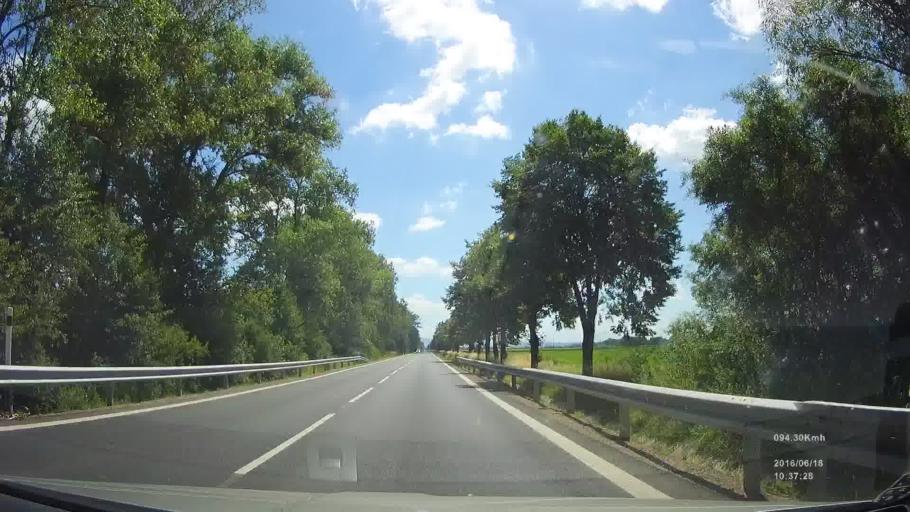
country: SK
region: Kosicky
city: Sobrance
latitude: 48.7639
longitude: 22.1070
